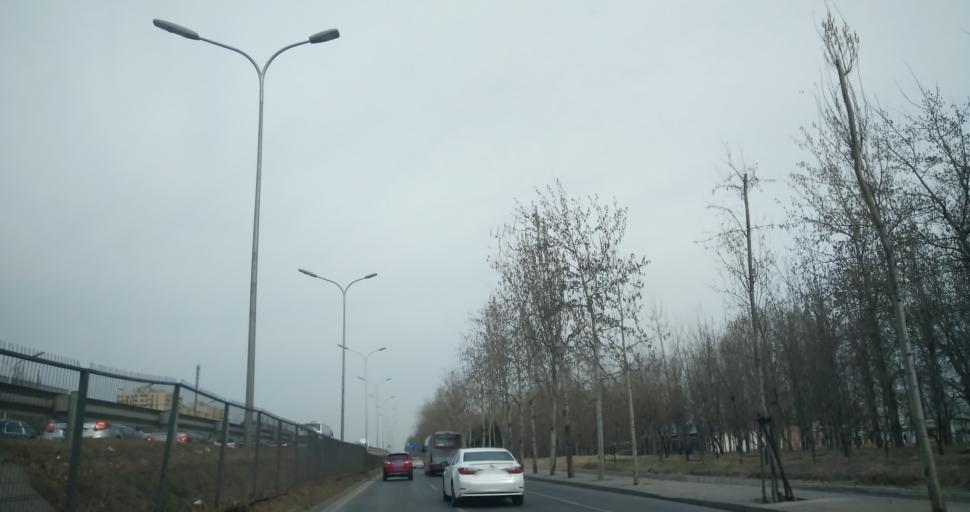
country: CN
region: Beijing
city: Dahongmen
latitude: 39.8298
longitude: 116.3691
